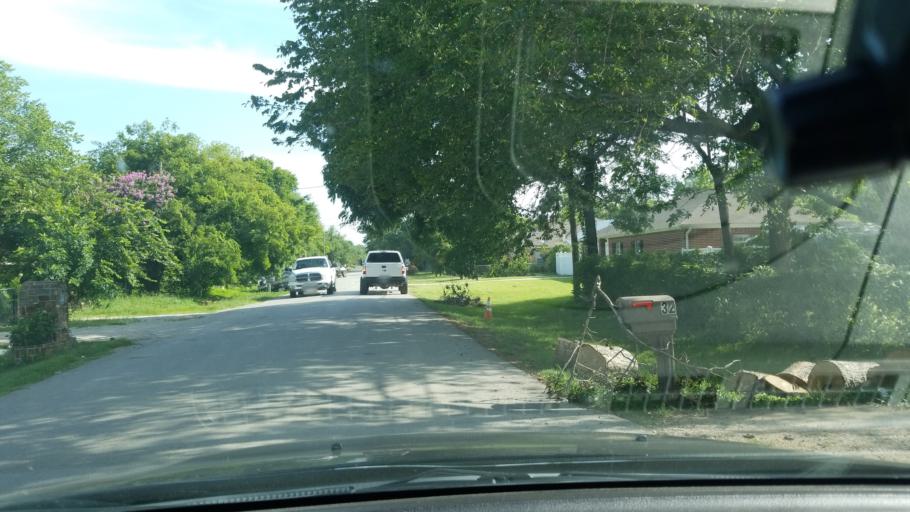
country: US
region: Texas
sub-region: Dallas County
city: Balch Springs
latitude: 32.7149
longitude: -96.6388
